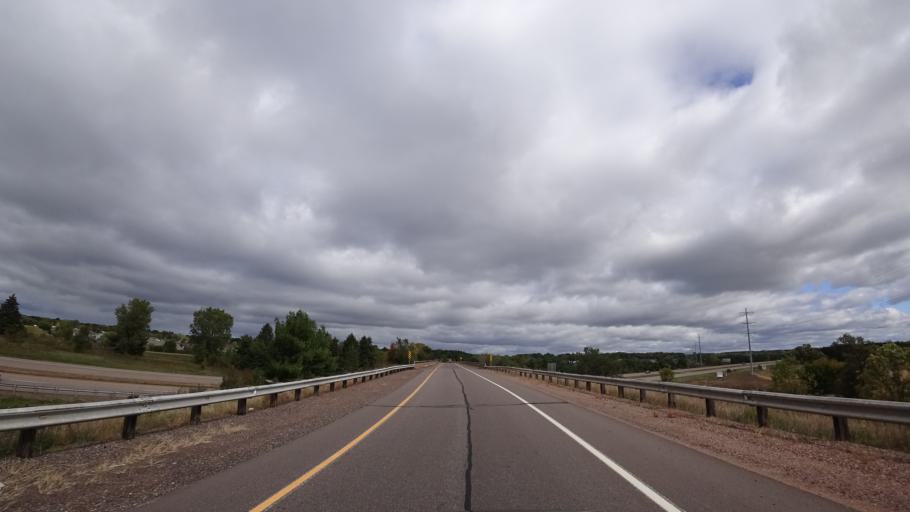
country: US
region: Wisconsin
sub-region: Chippewa County
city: Lake Wissota
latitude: 44.9191
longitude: -91.3377
